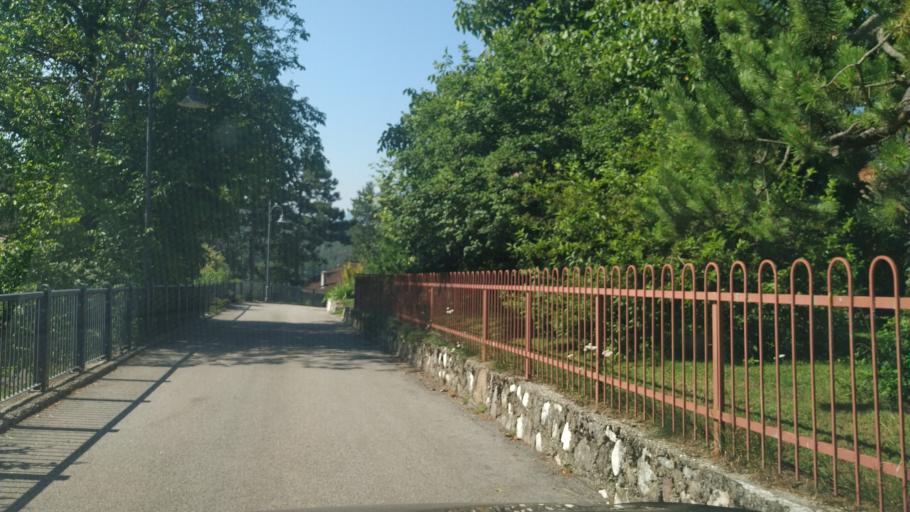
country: IT
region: Trentino-Alto Adige
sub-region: Provincia di Trento
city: Sanzeno
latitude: 46.3673
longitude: 11.0787
